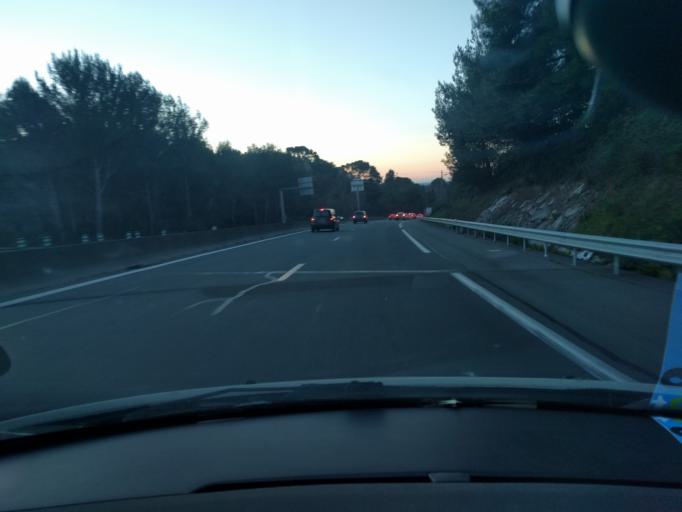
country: FR
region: Provence-Alpes-Cote d'Azur
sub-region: Departement des Alpes-Maritimes
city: Mougins
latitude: 43.6015
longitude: 7.0026
